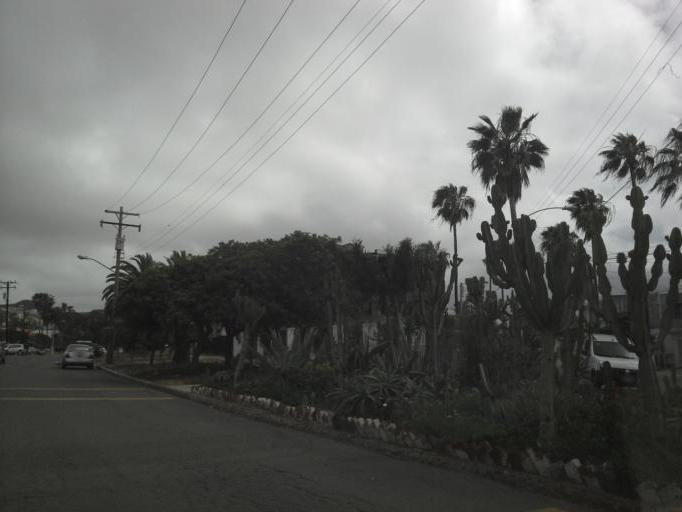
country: US
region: California
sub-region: San Diego County
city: Imperial Beach
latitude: 32.5292
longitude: -117.1131
